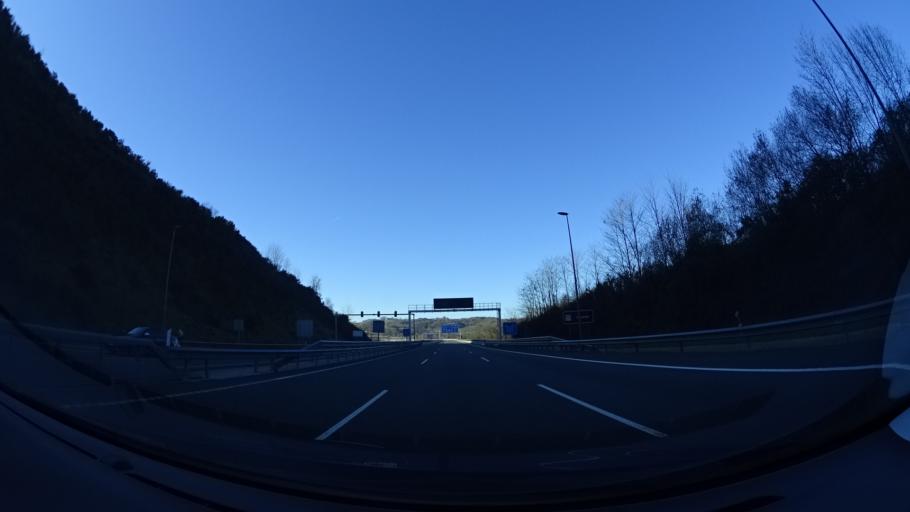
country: ES
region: Basque Country
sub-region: Provincia de Guipuzcoa
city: Astigarraga
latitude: 43.2895
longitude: -1.9432
